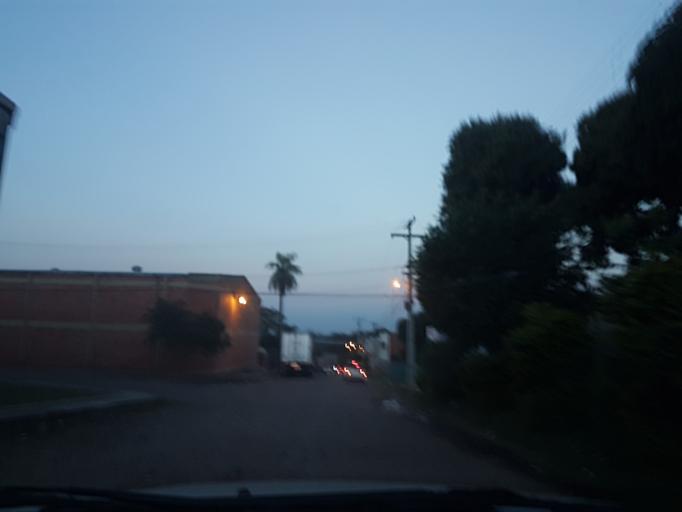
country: PY
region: Central
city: Colonia Mariano Roque Alonso
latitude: -25.2277
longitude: -57.5282
